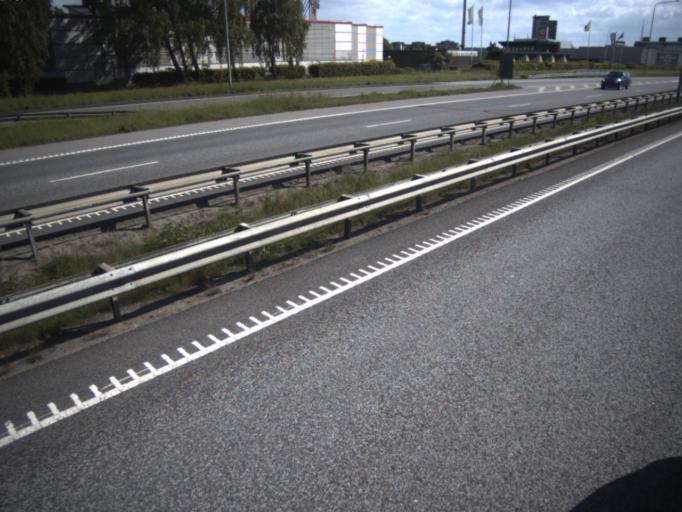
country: SE
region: Skane
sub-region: Helsingborg
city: Helsingborg
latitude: 56.0661
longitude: 12.7186
